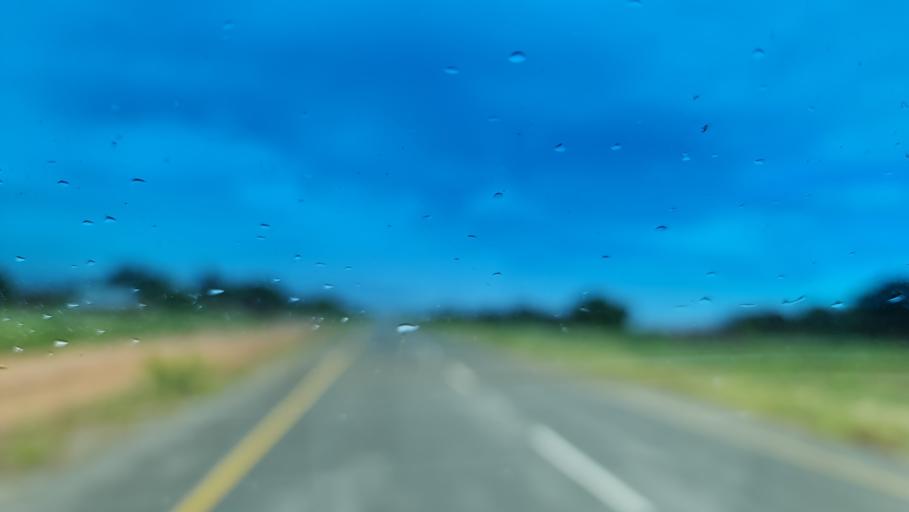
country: MZ
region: Nampula
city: Nampula
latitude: -15.5552
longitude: 39.3222
